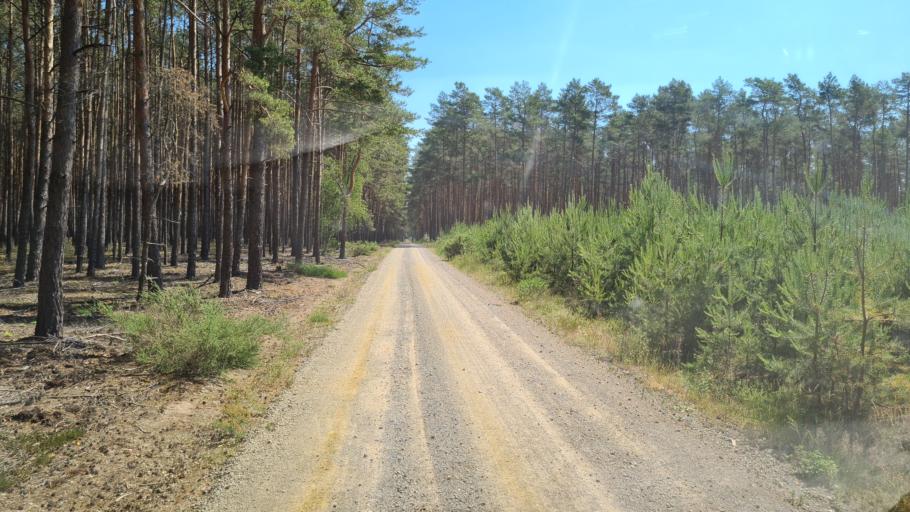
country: DE
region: Brandenburg
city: Schlieben
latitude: 51.7797
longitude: 13.3516
